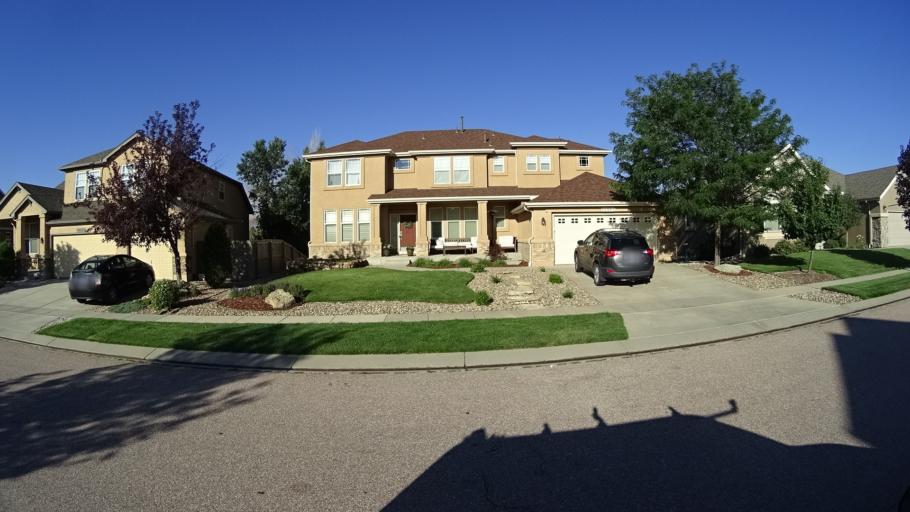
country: US
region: Colorado
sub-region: El Paso County
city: Black Forest
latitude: 38.9847
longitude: -104.7726
